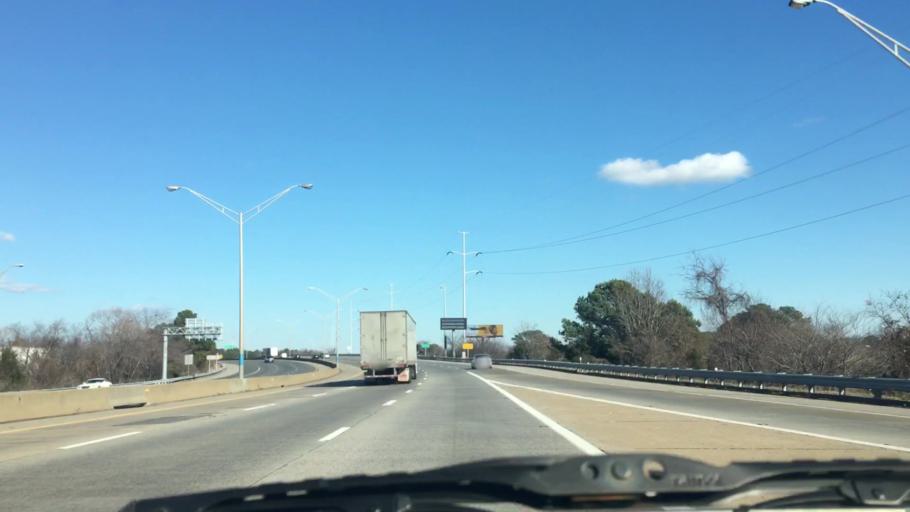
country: US
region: Virginia
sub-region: City of Newport News
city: Newport News
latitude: 36.9935
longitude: -76.4032
